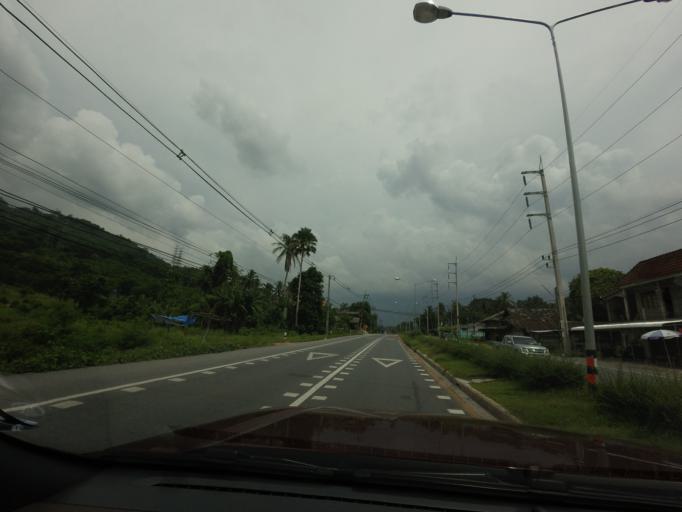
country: TH
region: Yala
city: Yala
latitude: 6.4815
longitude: 101.2657
